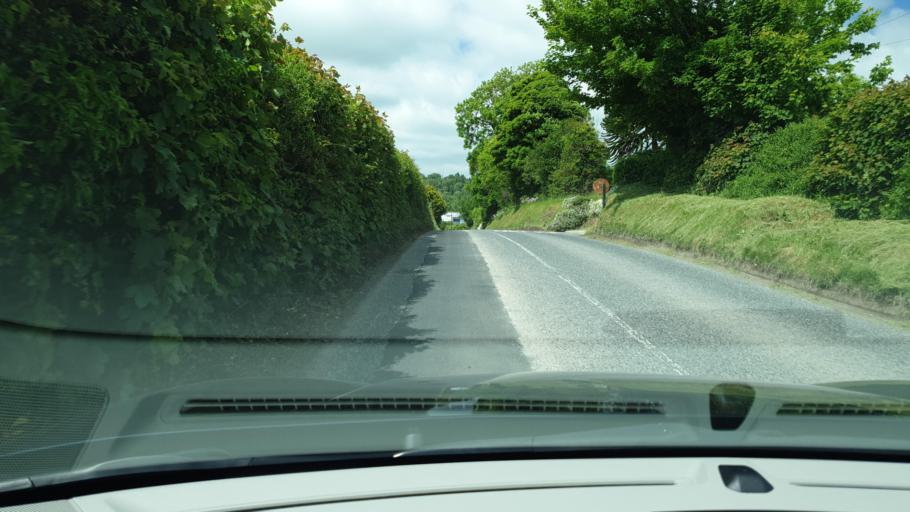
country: IE
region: Ulster
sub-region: An Cabhan
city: Kingscourt
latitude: 53.9020
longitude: -6.7805
